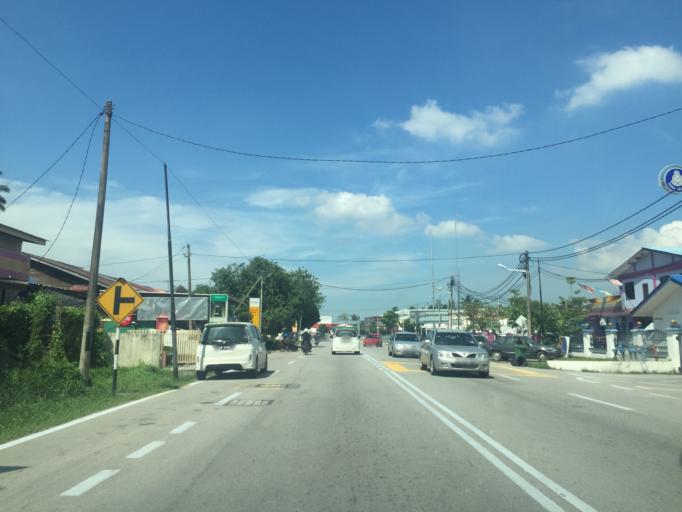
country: MY
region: Penang
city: Tasek Glugor
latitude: 5.4834
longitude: 100.4910
